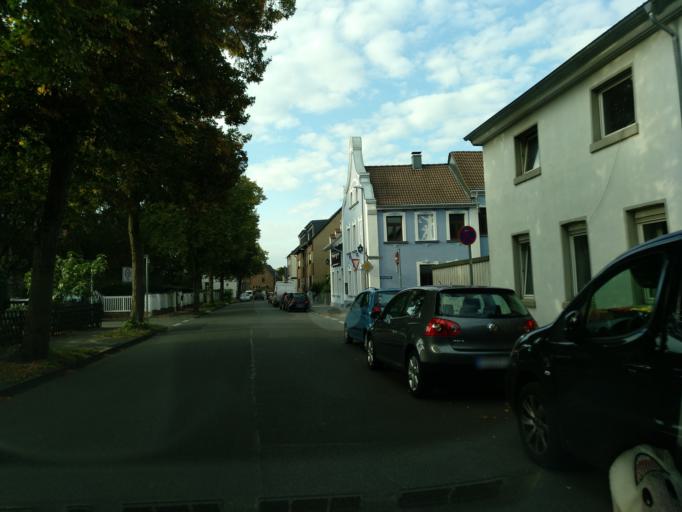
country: DE
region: North Rhine-Westphalia
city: Tonisvorst
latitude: 51.3759
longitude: 6.5068
